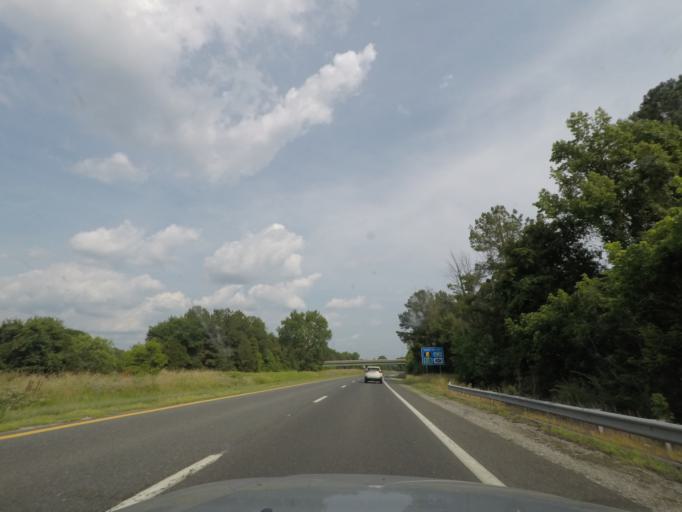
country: US
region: Virginia
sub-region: Prince Edward County
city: Farmville
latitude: 37.2824
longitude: -78.4286
